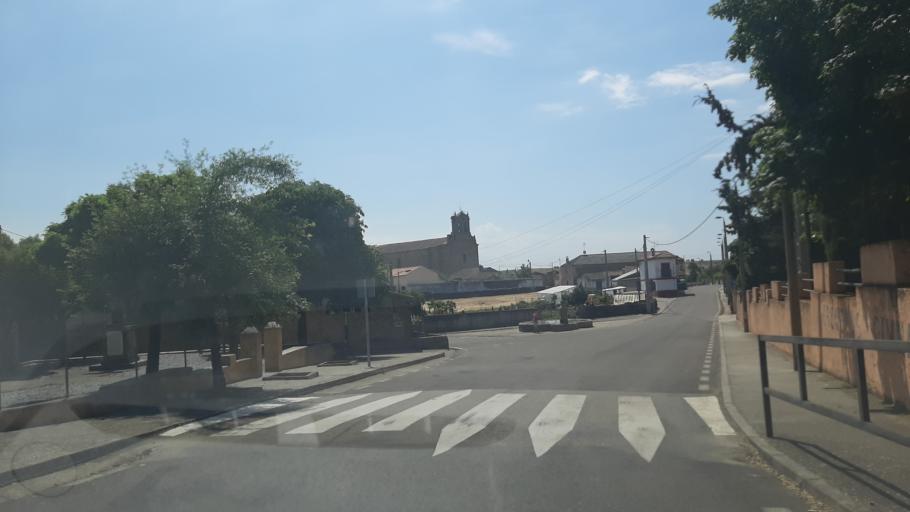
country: ES
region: Castille and Leon
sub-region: Provincia de Salamanca
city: Gallegos de Arganan
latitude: 40.6320
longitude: -6.7059
